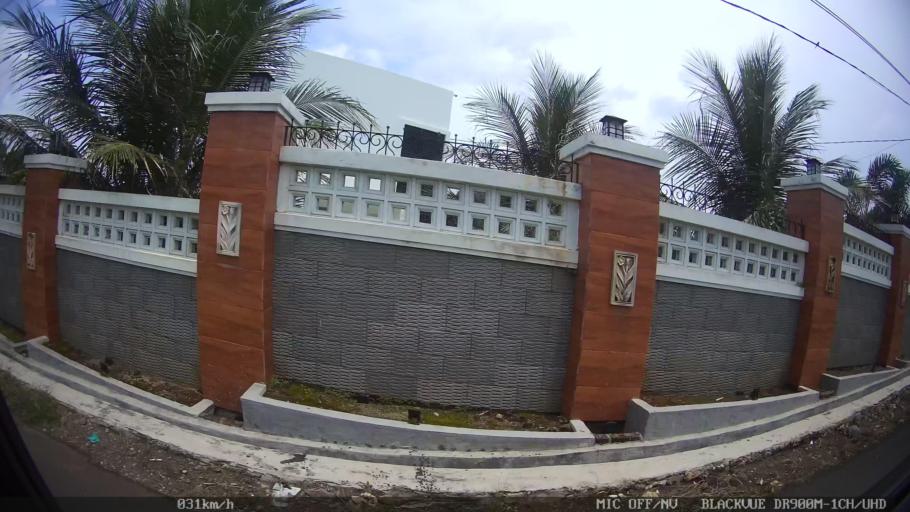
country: ID
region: Lampung
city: Bandarlampung
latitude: -5.4148
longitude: 105.2152
